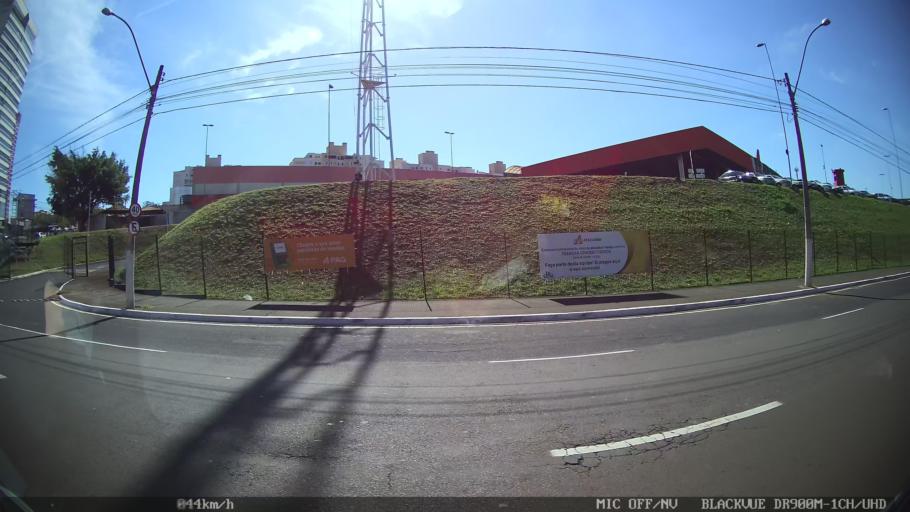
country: BR
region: Sao Paulo
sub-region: Franca
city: Franca
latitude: -20.5537
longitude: -47.4126
